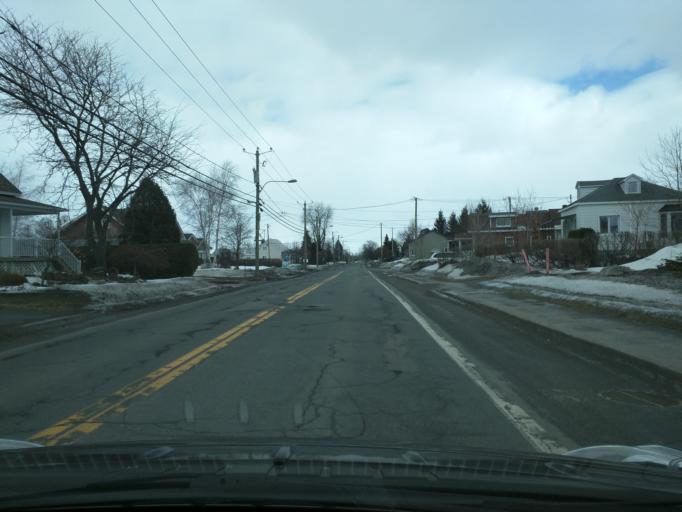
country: CA
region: Quebec
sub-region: Monteregie
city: Sainte-Julie
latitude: 45.6539
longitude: -73.2941
